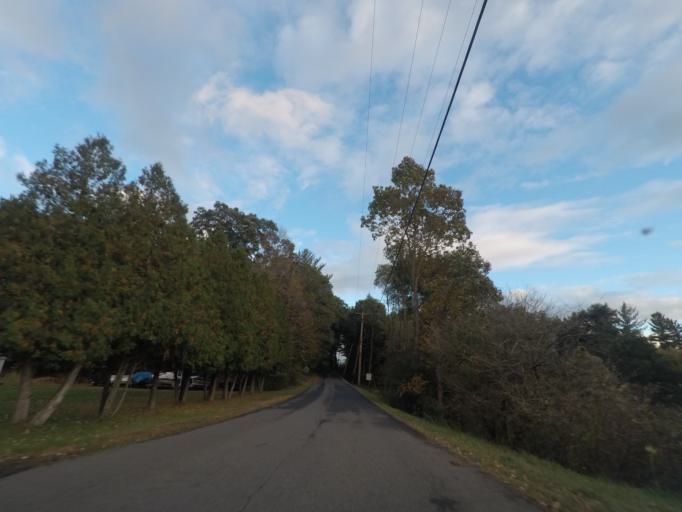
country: US
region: New York
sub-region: Rensselaer County
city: Nassau
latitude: 42.5538
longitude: -73.5954
